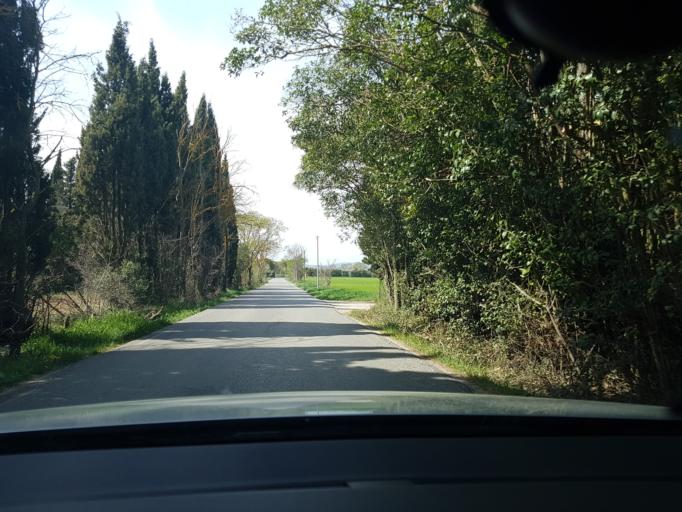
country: FR
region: Provence-Alpes-Cote d'Azur
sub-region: Departement des Bouches-du-Rhone
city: Bouc-Bel-Air
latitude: 43.4738
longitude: 5.3955
